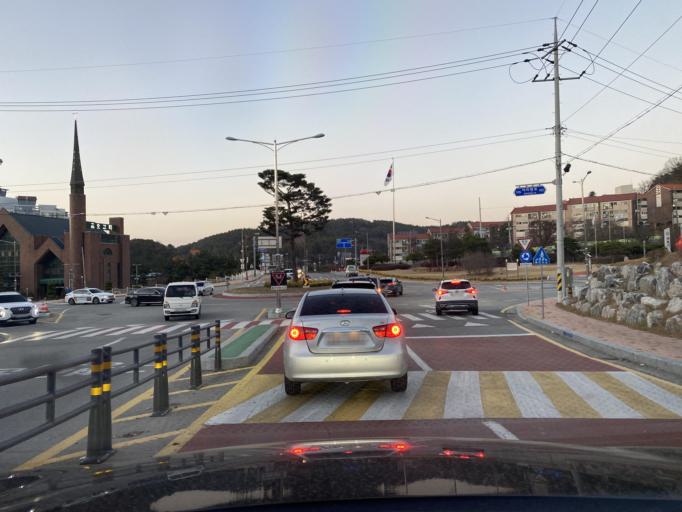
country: KR
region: Chungcheongnam-do
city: Yesan
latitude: 36.6863
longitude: 126.8431
